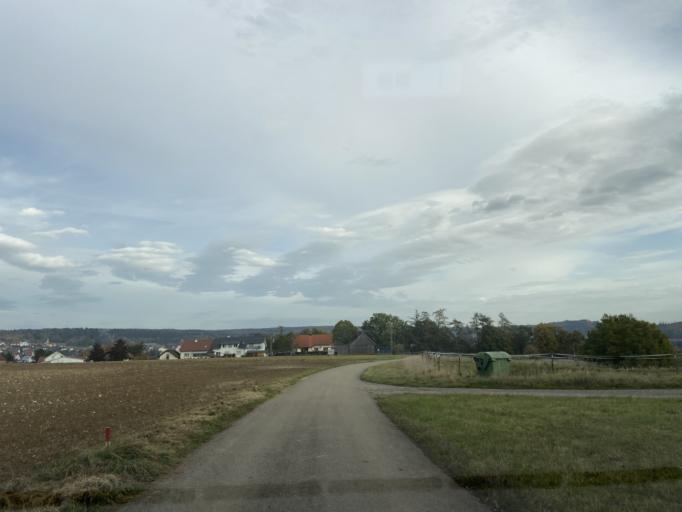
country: DE
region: Baden-Wuerttemberg
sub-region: Tuebingen Region
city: Bingen
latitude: 48.1052
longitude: 9.2742
